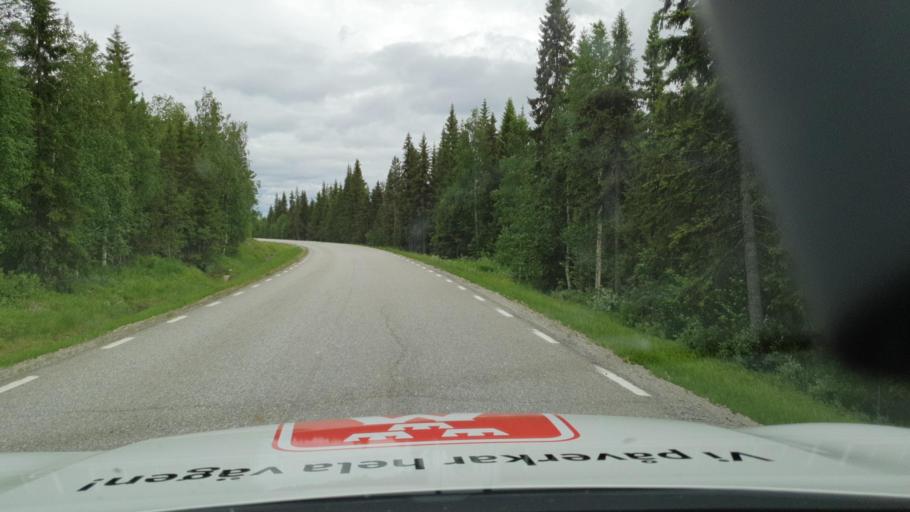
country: SE
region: Vaesterbotten
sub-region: Lycksele Kommun
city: Soderfors
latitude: 64.3169
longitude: 18.1574
